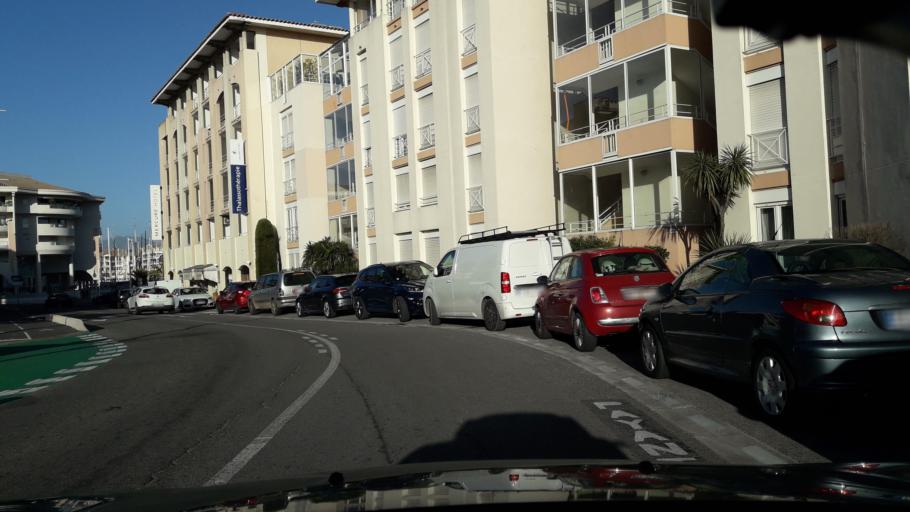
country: FR
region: Provence-Alpes-Cote d'Azur
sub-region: Departement du Var
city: Frejus
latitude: 43.4197
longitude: 6.7459
